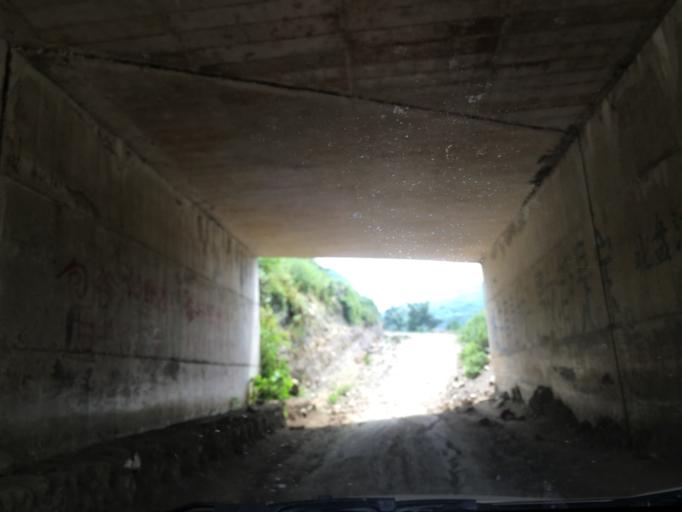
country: CN
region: Guizhou Sheng
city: Anshun
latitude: 25.5997
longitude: 105.6635
